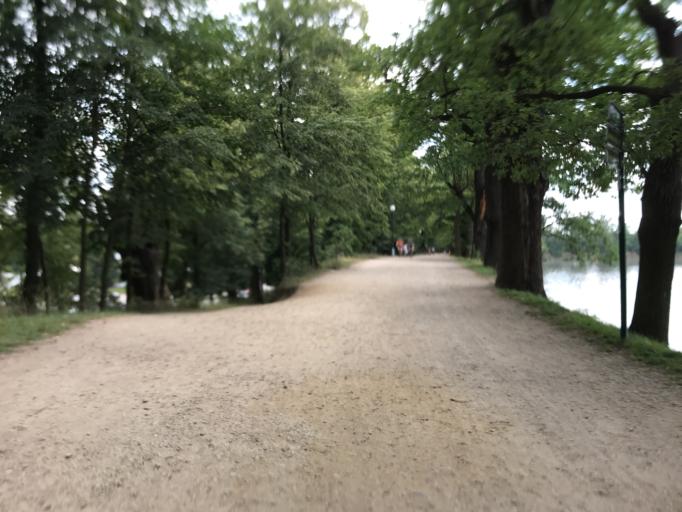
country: CZ
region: Jihocesky
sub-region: Okres Jindrichuv Hradec
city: Trebon
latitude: 49.0009
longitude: 14.7719
